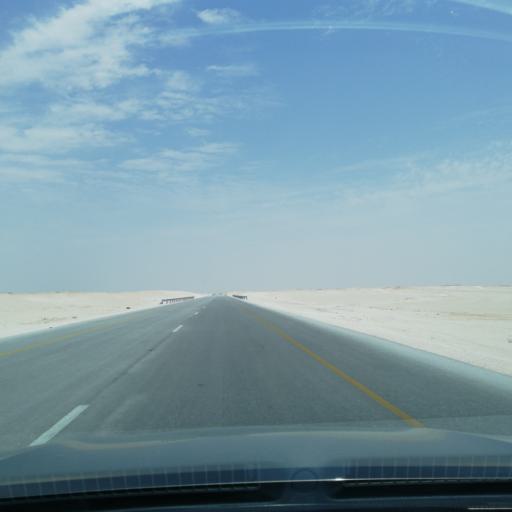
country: OM
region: Al Wusta
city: Hayma'
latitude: 19.6127
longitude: 55.5739
